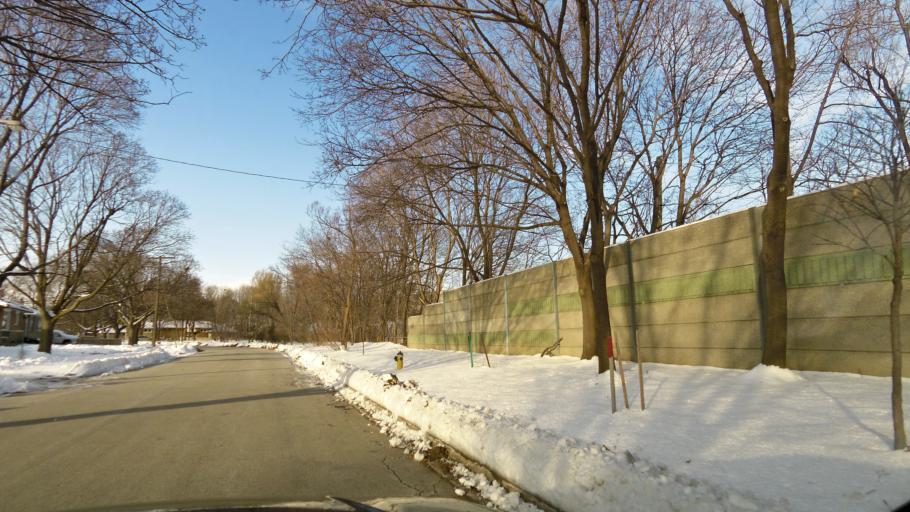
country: CA
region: Ontario
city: Etobicoke
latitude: 43.6677
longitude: -79.5744
